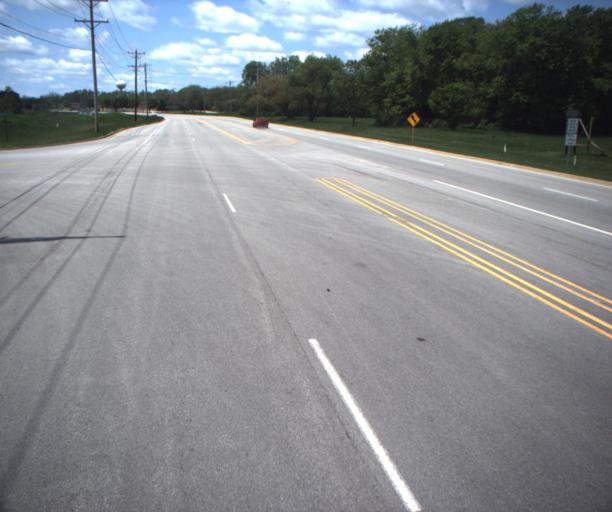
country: US
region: Illinois
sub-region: Kane County
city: Geneva
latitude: 41.8710
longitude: -88.2631
